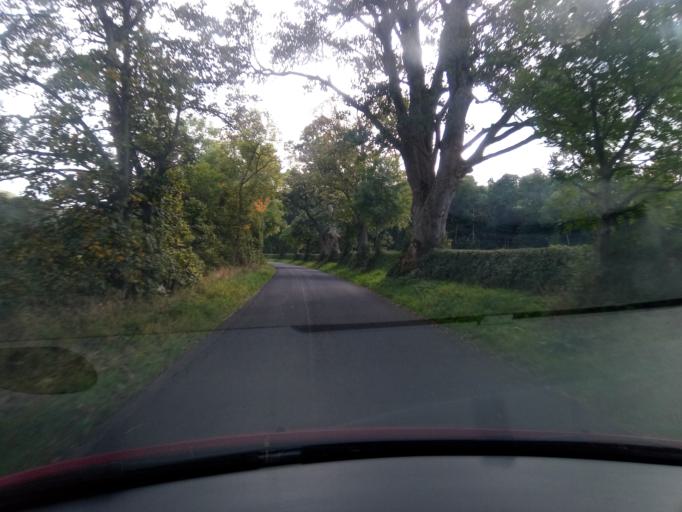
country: GB
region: Scotland
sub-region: The Scottish Borders
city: Kelso
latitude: 55.5078
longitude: -2.3515
